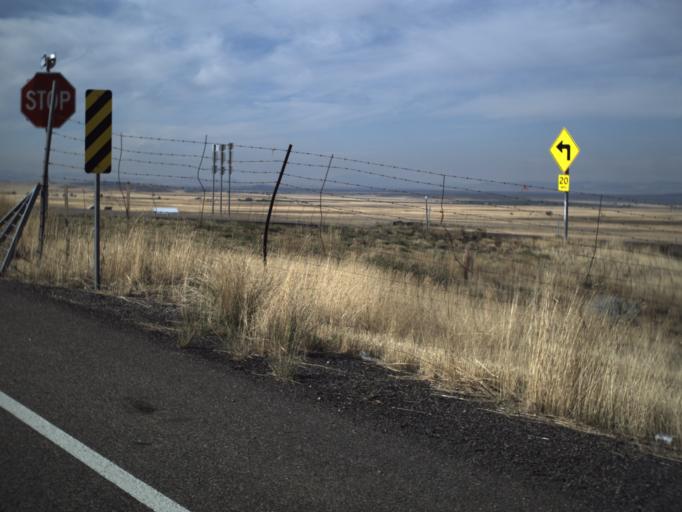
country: US
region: Utah
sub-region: Millard County
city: Fillmore
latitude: 39.1451
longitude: -112.2371
